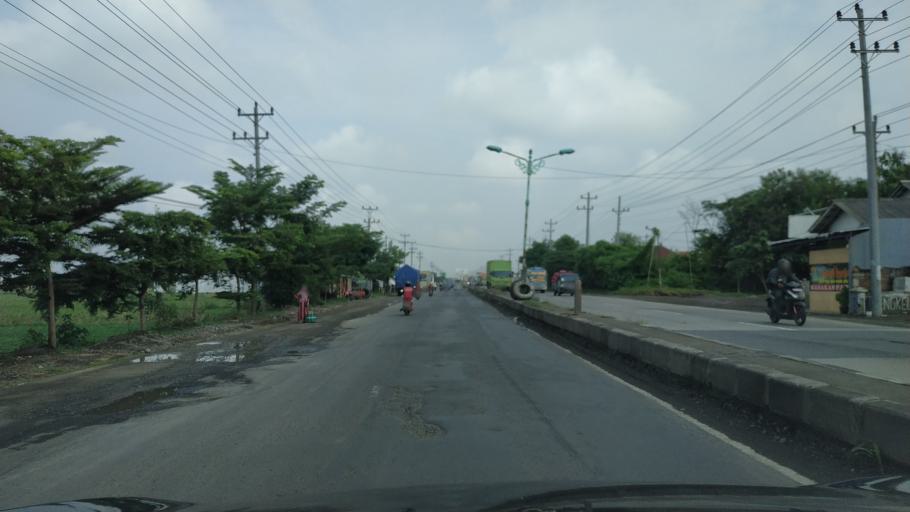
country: ID
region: Central Java
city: Bulakamba
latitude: -6.8720
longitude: 108.9030
